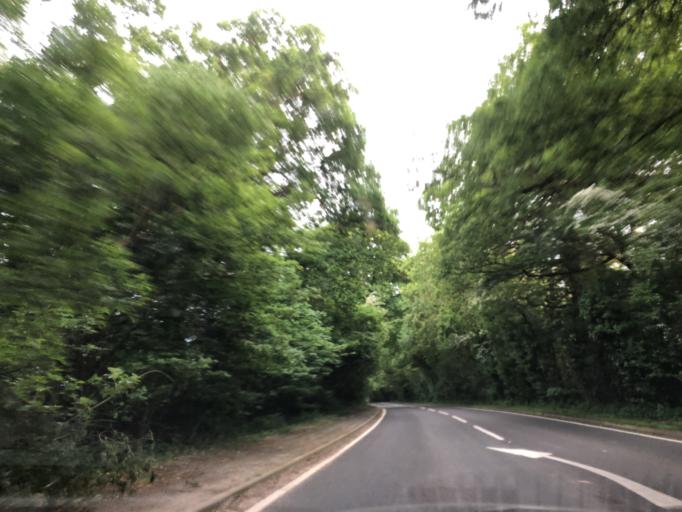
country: GB
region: England
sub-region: Warwickshire
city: Wroxall
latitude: 52.3206
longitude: -1.6665
